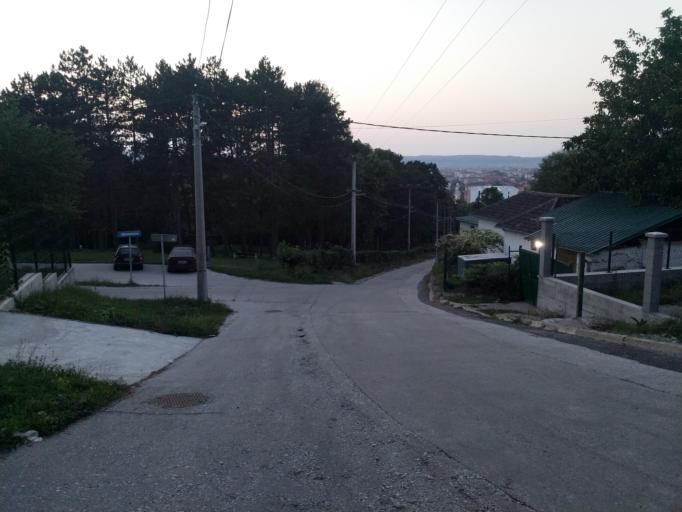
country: RS
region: Central Serbia
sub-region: Pomoravski Okrug
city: Jagodina
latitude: 43.9624
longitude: 21.2687
